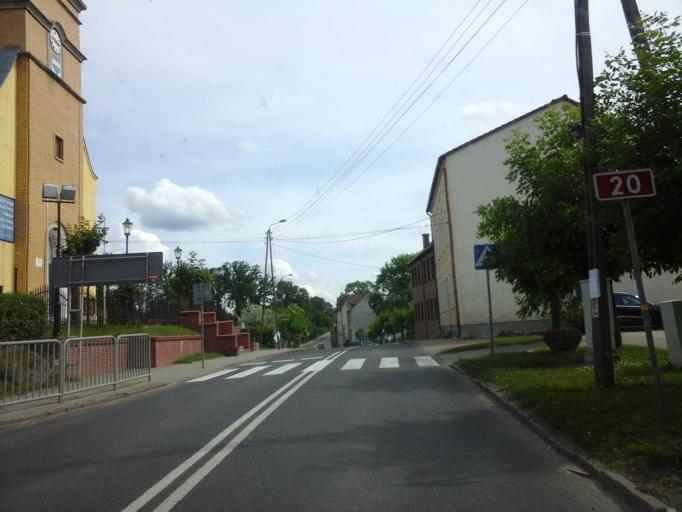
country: PL
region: West Pomeranian Voivodeship
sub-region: Powiat lobeski
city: Wegorzyno
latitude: 53.5374
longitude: 15.5576
